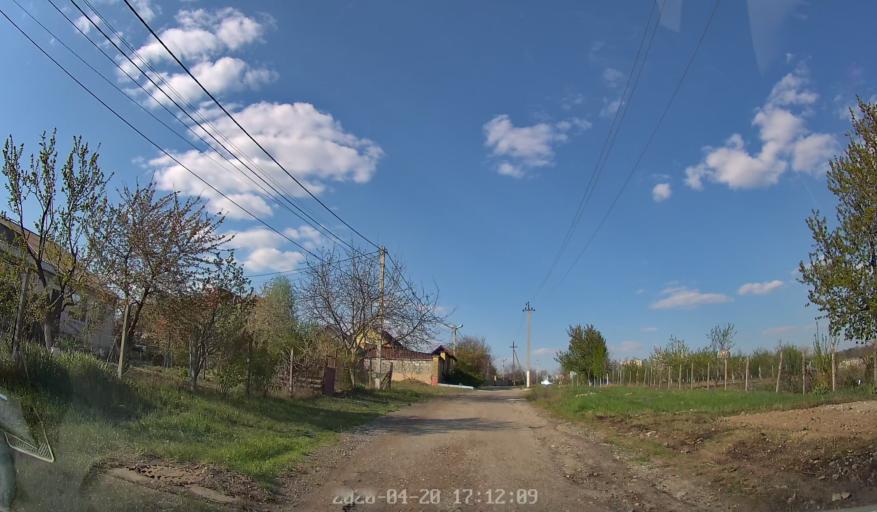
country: MD
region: Chisinau
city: Chisinau
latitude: 46.9646
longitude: 28.8417
